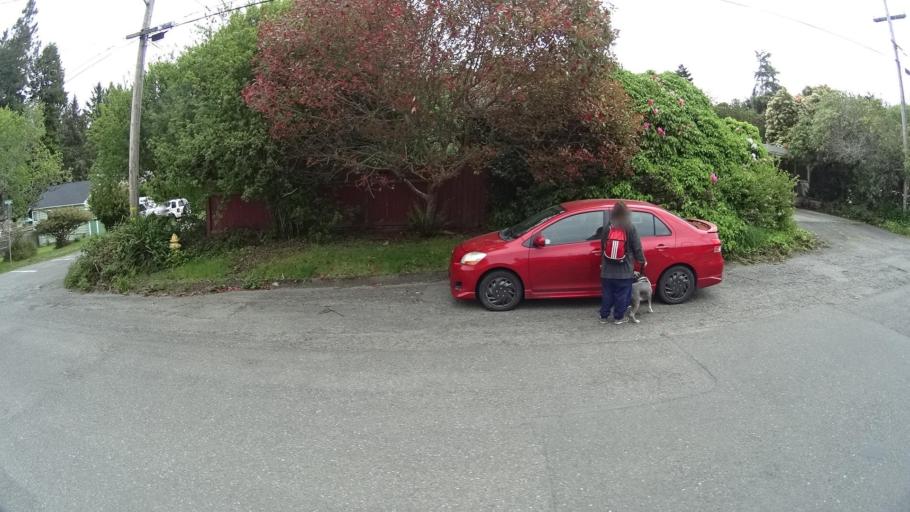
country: US
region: California
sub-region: Humboldt County
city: Cutten
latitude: 40.7710
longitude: -124.1477
